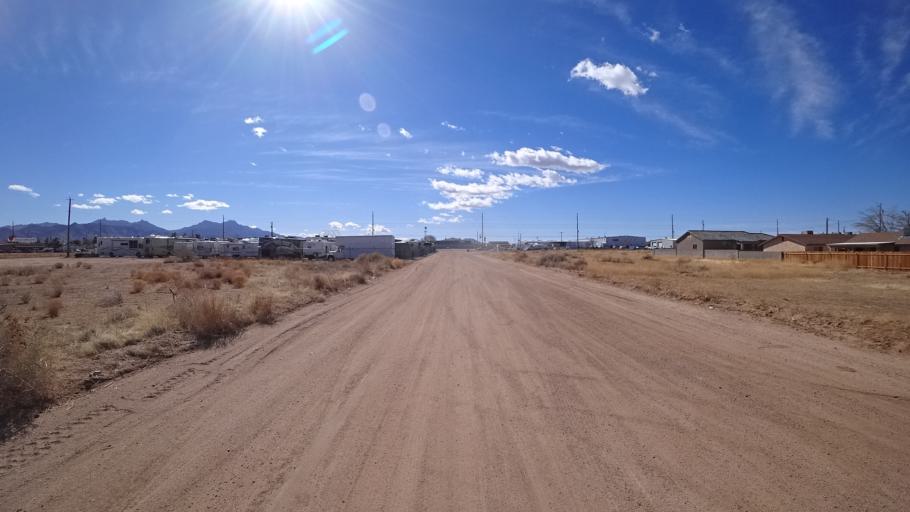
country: US
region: Arizona
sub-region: Mohave County
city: New Kingman-Butler
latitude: 35.2264
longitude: -114.0174
